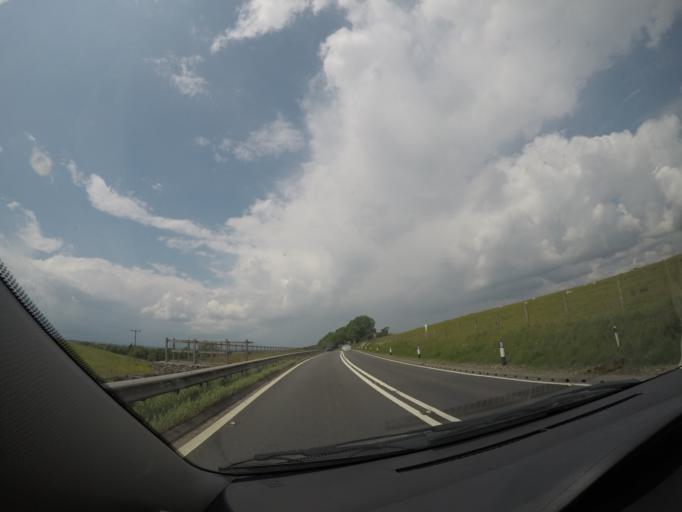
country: GB
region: England
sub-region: Cumbria
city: Kirkby Stephen
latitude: 54.5445
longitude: -2.4015
